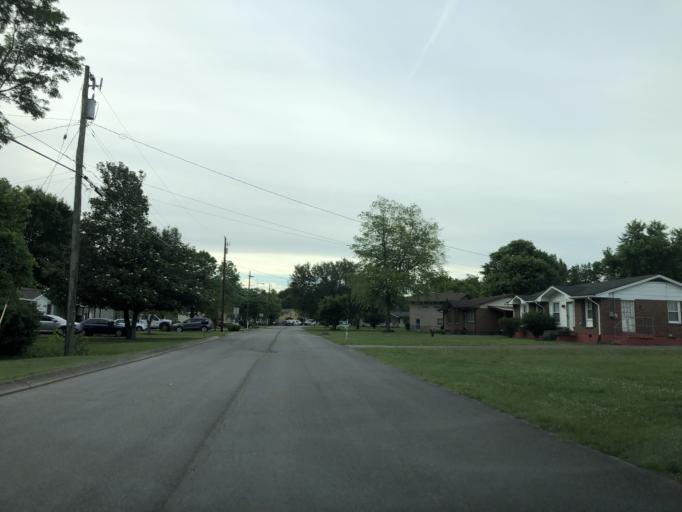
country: US
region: Tennessee
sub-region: Davidson County
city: Goodlettsville
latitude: 36.2904
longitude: -86.7175
